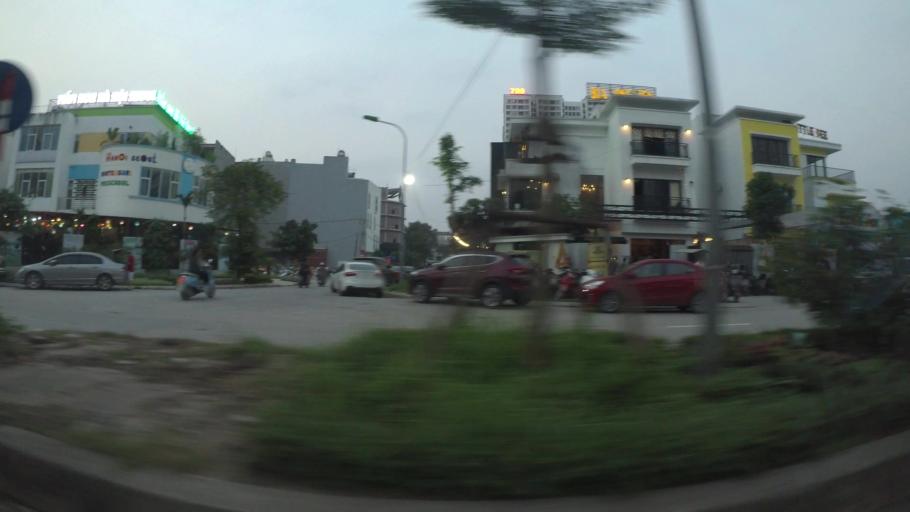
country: VN
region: Ha Noi
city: Tay Ho
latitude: 21.0675
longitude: 105.7968
